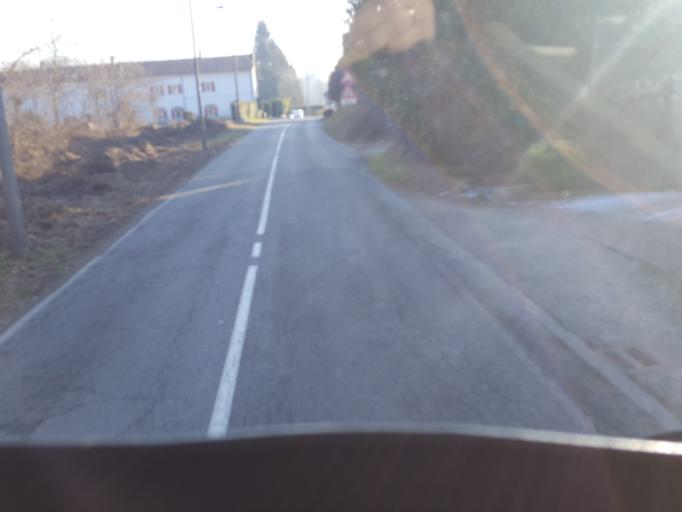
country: IT
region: Piedmont
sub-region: Provincia di Novara
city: Varallo Pombia
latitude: 45.6846
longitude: 8.6311
